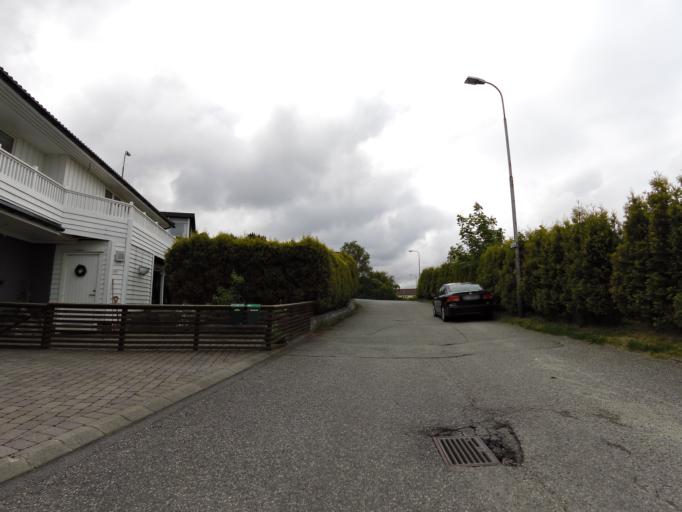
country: NO
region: Rogaland
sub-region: Randaberg
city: Randaberg
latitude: 58.9538
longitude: 5.6600
